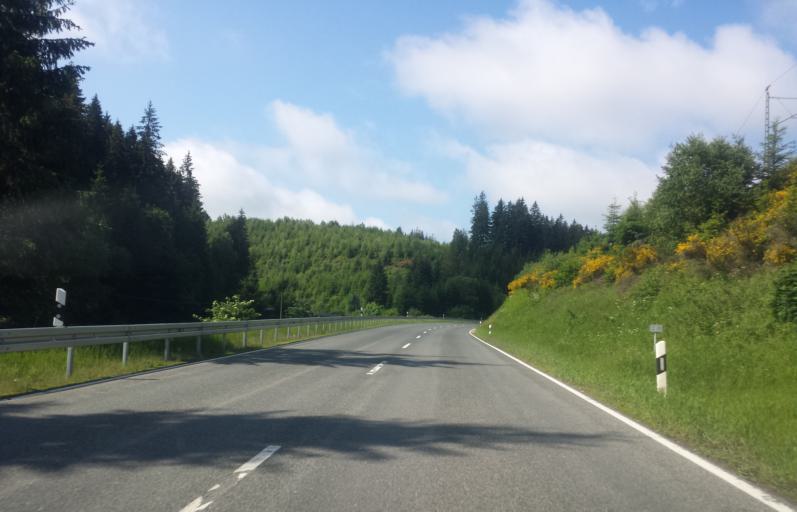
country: DE
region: Bavaria
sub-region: Upper Franconia
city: Ludwigsstadt
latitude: 50.4633
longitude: 11.3805
